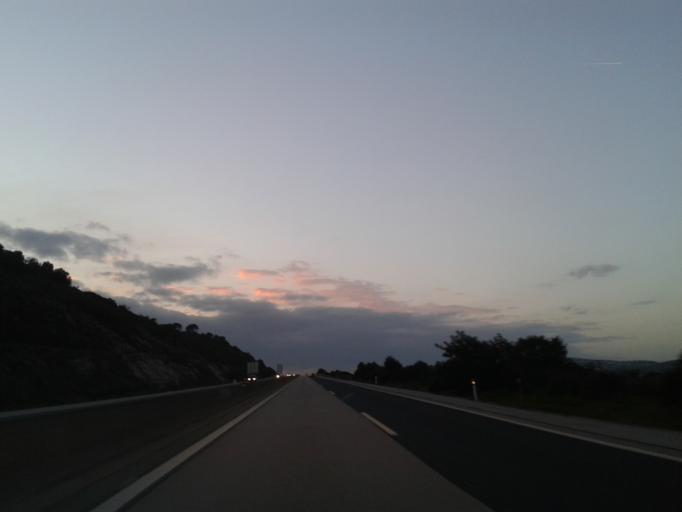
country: PT
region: Faro
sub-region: Loule
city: Loule
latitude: 37.1215
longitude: -8.0608
